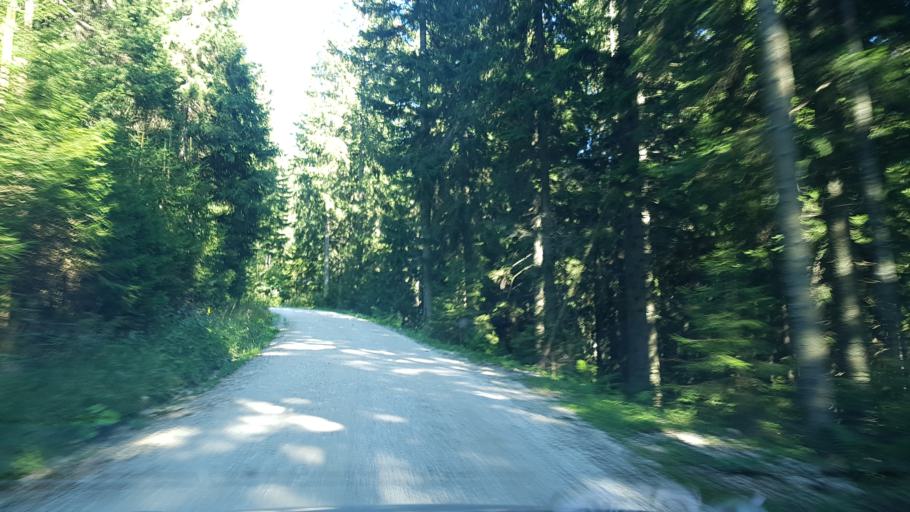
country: SI
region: Ravne na Koroskem
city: Kotlje
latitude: 46.4784
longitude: 14.9553
